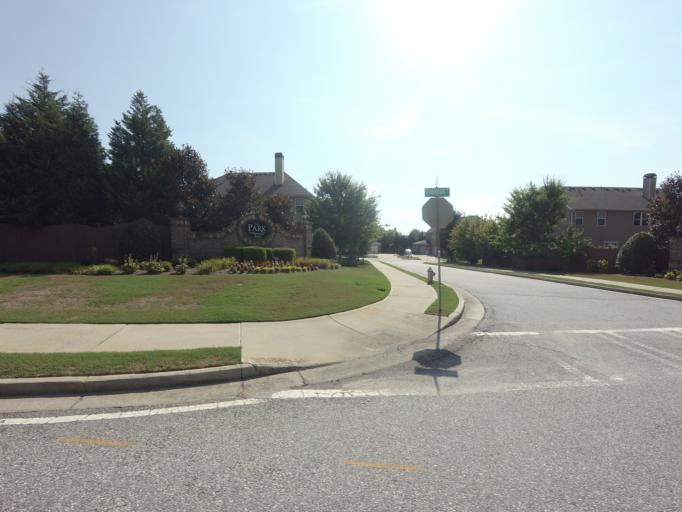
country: US
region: Georgia
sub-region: Fulton County
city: Johns Creek
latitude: 34.0860
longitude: -84.2058
